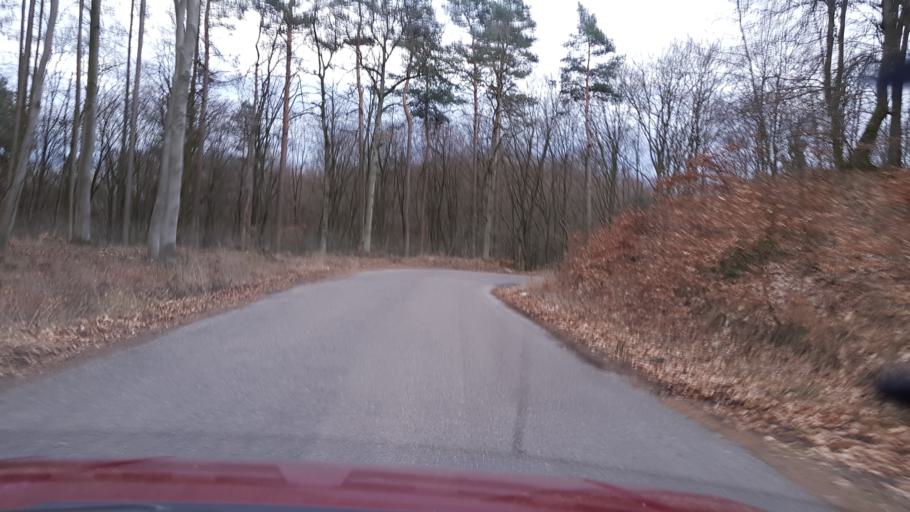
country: PL
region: West Pomeranian Voivodeship
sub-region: Szczecin
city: Szczecin
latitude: 53.3430
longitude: 14.6280
